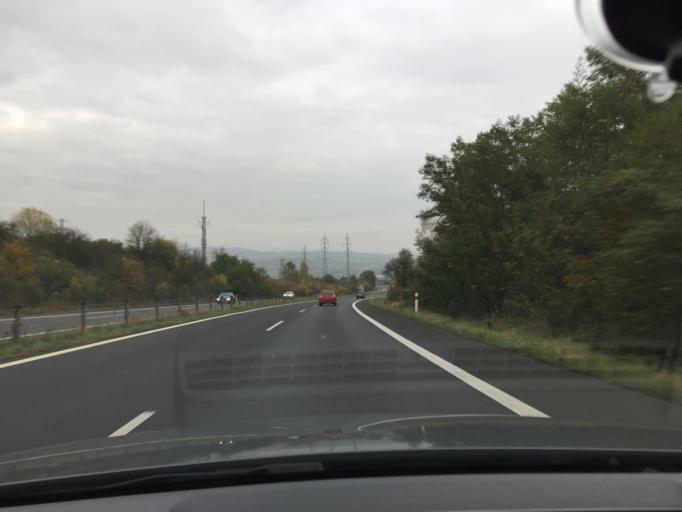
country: CZ
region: Ustecky
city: Rehlovice
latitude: 50.6152
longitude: 13.9183
